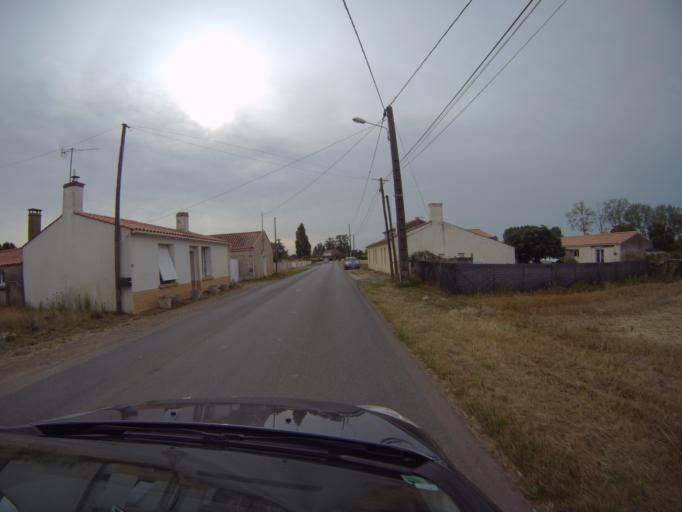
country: FR
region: Pays de la Loire
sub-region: Departement de la Vendee
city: Angles
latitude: 46.4085
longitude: -1.4429
